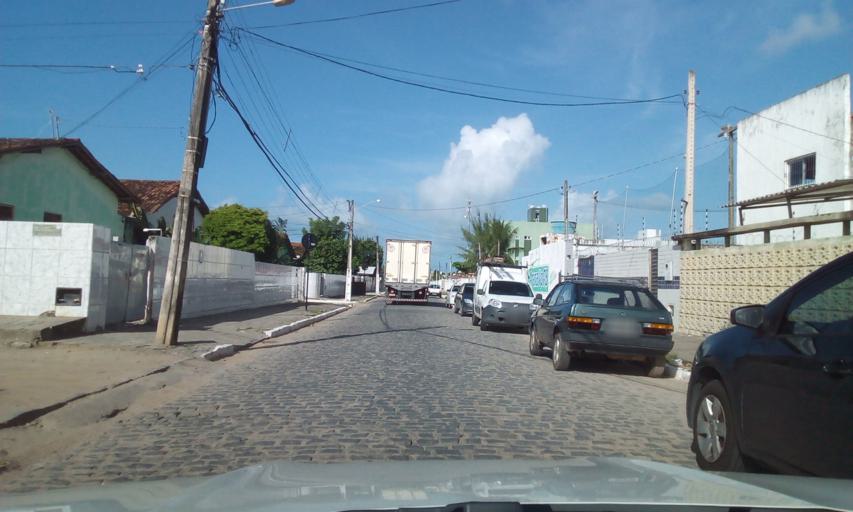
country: BR
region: Paraiba
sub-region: Joao Pessoa
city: Joao Pessoa
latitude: -7.1739
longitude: -34.8717
